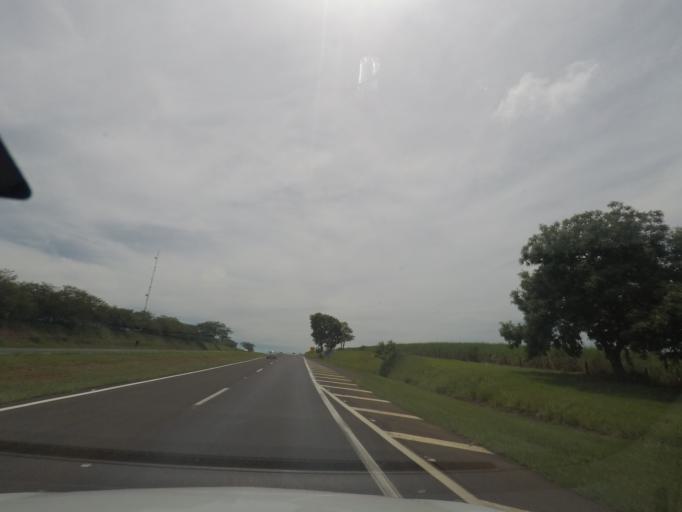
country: BR
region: Sao Paulo
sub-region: Bebedouro
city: Bebedouro
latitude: -20.9697
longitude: -48.4404
